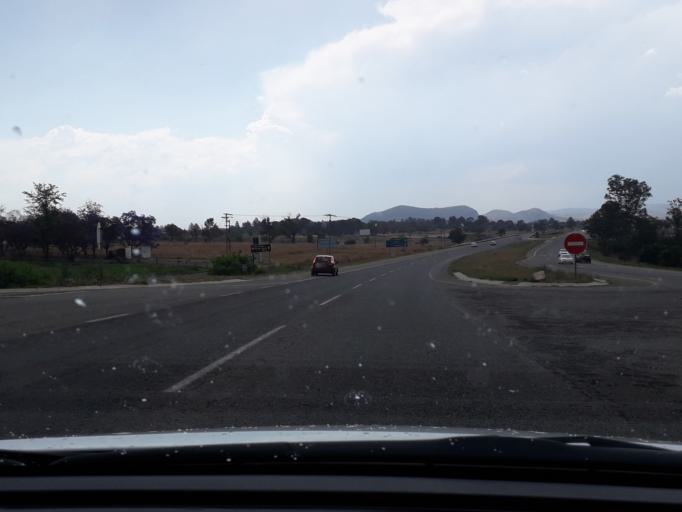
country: ZA
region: Gauteng
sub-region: West Rand District Municipality
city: Muldersdriseloop
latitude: -26.0243
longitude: 27.8624
